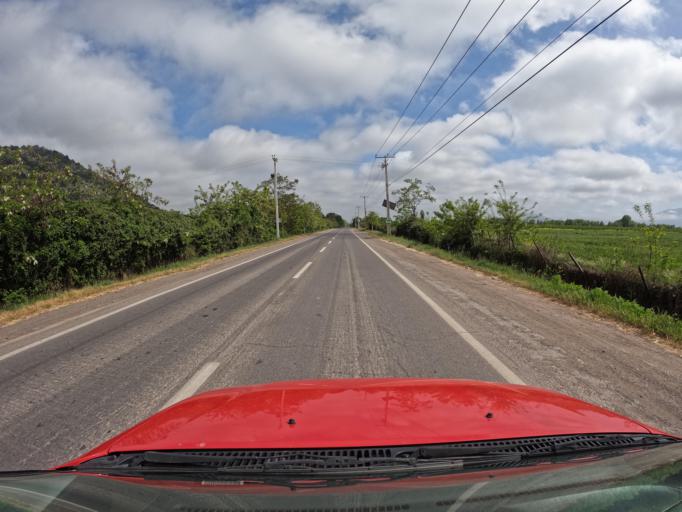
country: CL
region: O'Higgins
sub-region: Provincia de Colchagua
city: Santa Cruz
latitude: -34.7050
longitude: -71.3030
